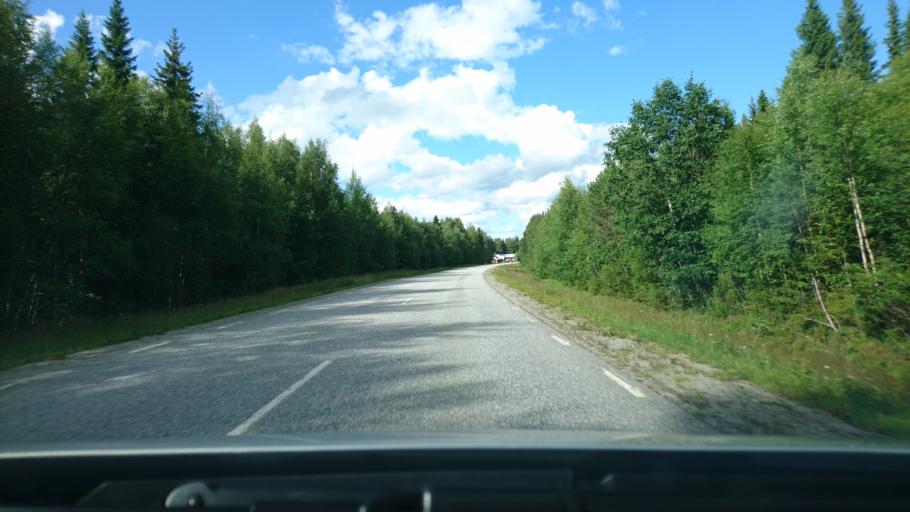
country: SE
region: Vaesterbotten
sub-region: Asele Kommun
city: Asele
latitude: 63.9937
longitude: 17.2640
